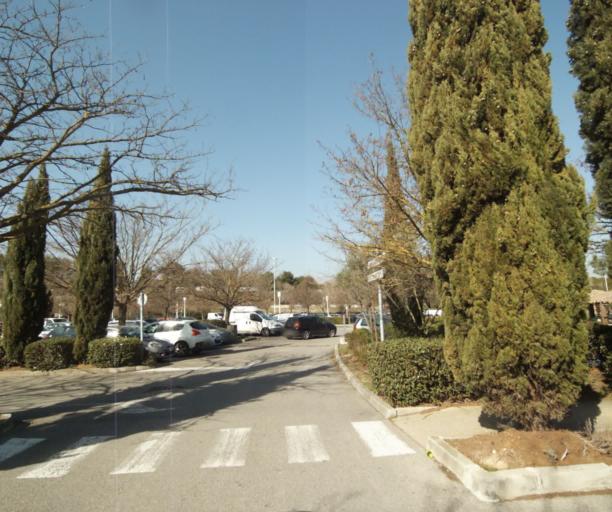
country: FR
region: Provence-Alpes-Cote d'Azur
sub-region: Departement des Bouches-du-Rhone
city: Cabries
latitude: 43.4313
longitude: 5.3970
